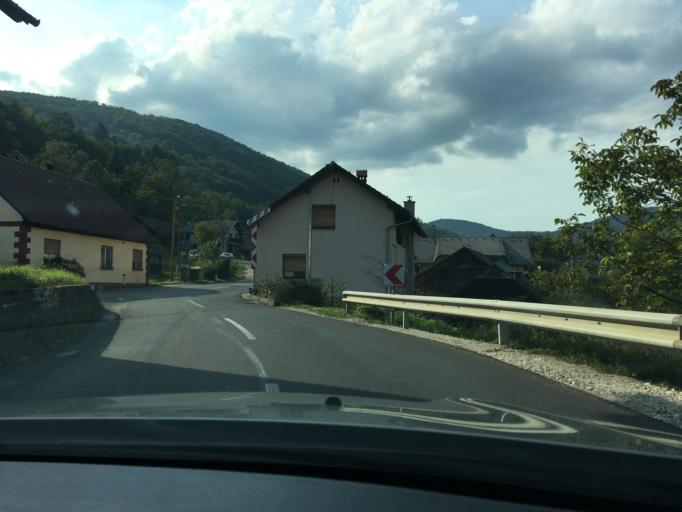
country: SI
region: Dolenjske Toplice
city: Dolenjske Toplice
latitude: 45.7606
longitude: 15.0310
